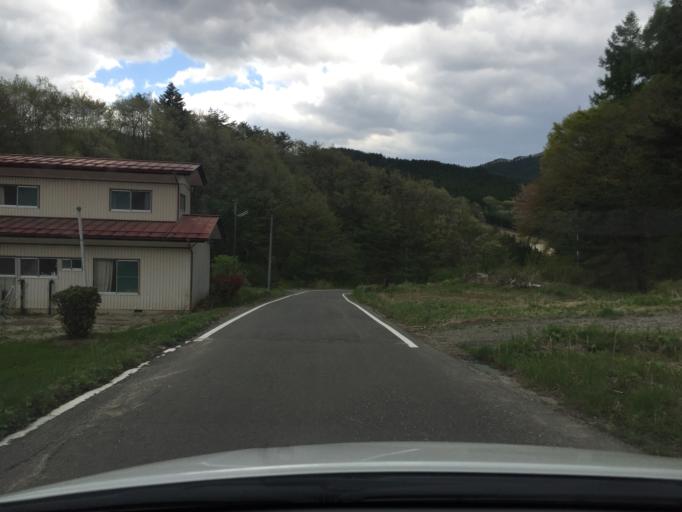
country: JP
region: Fukushima
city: Yanagawamachi-saiwaicho
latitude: 37.7573
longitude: 140.6987
